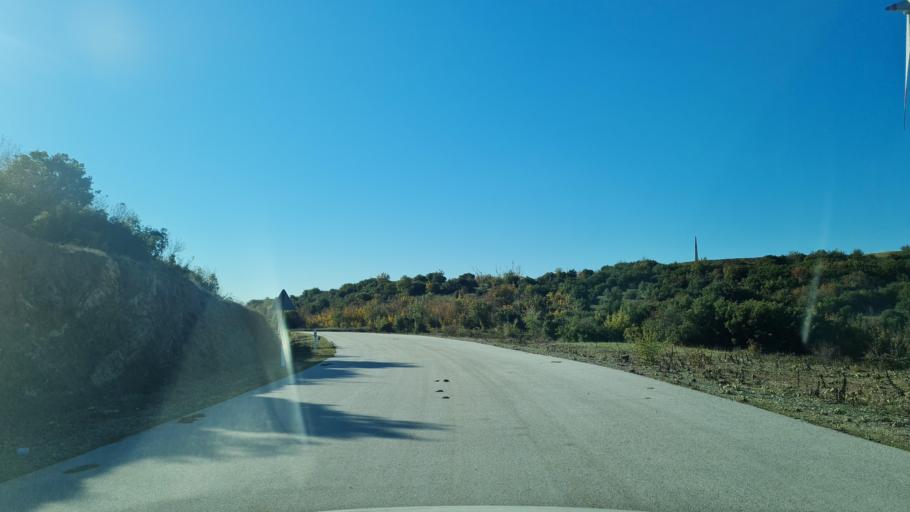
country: MK
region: Bogdanci
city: Bogdanci
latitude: 41.2232
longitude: 22.5513
